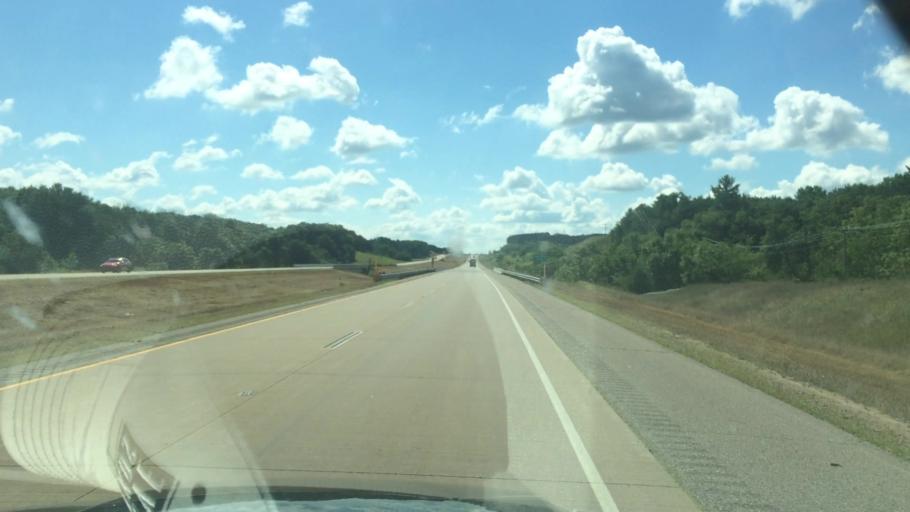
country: US
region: Wisconsin
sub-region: Portage County
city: Amherst
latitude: 44.4241
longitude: -89.2597
